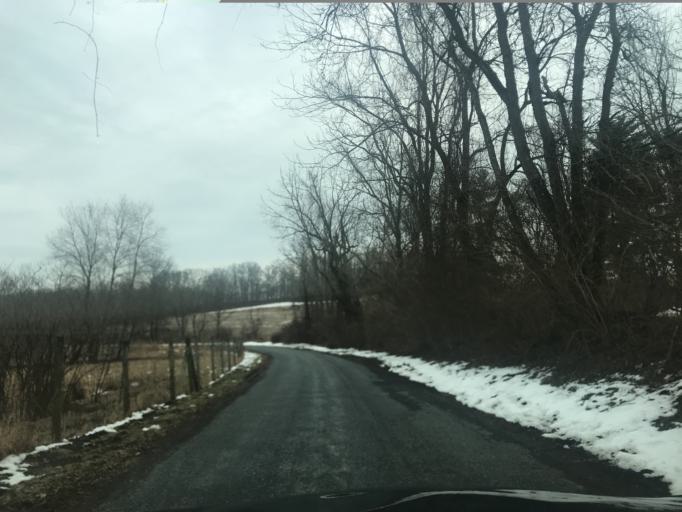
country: US
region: Pennsylvania
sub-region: York County
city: Stewartstown
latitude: 39.7010
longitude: -76.5124
